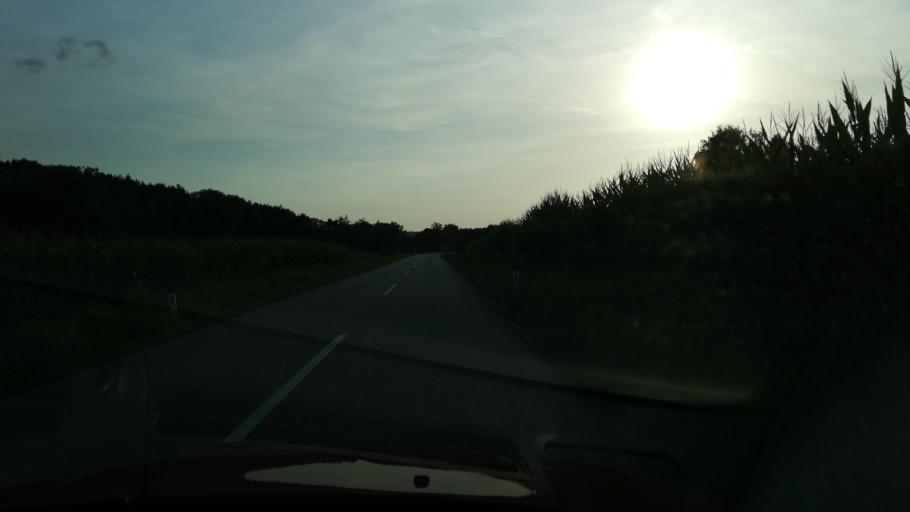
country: AT
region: Upper Austria
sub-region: Wels-Land
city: Edt bei Lambach
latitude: 48.1286
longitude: 13.9027
